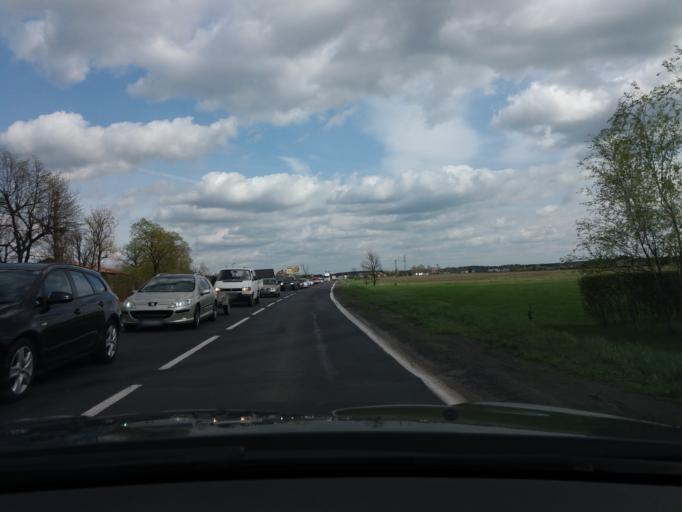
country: PL
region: Lower Silesian Voivodeship
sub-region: Powiat legnicki
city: Prochowice
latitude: 51.2704
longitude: 16.3663
